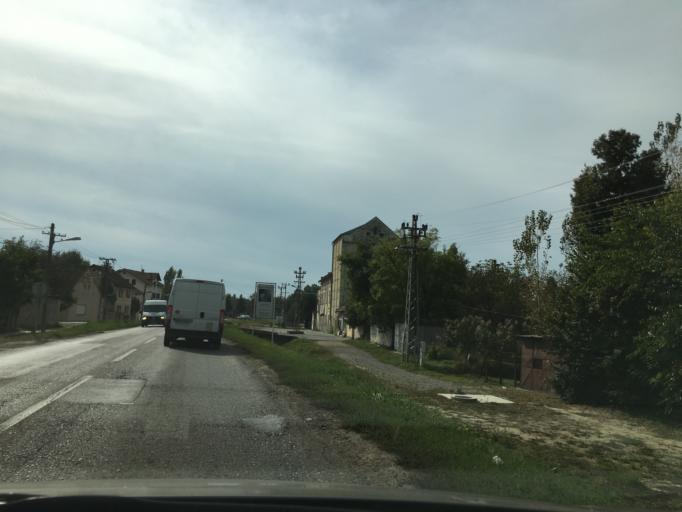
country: RS
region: Autonomna Pokrajina Vojvodina
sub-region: Juznobacki Okrug
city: Temerin
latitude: 45.3761
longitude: 19.8756
